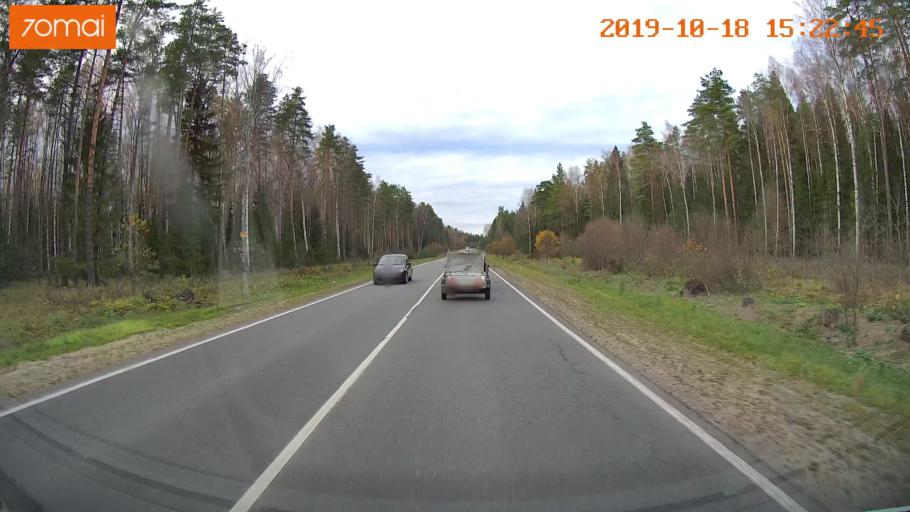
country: RU
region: Vladimir
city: Anopino
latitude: 55.7109
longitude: 40.7286
